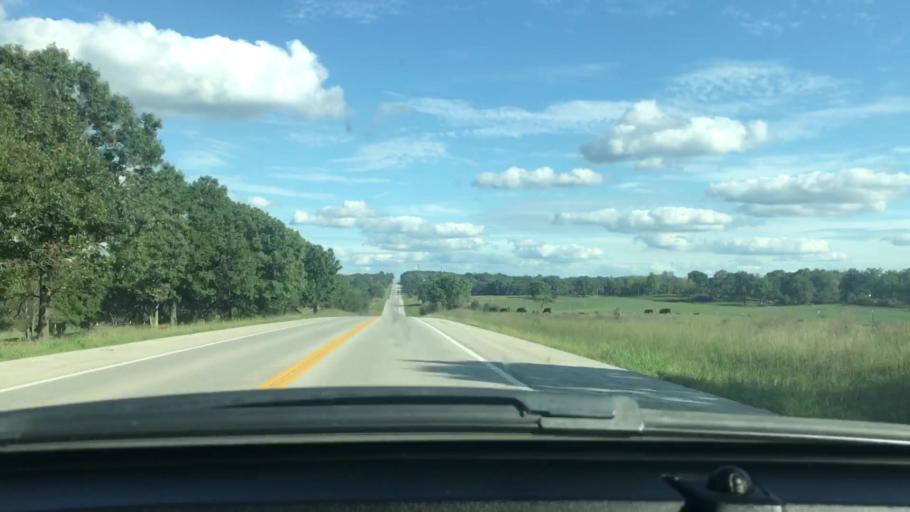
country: US
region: Missouri
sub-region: Howell County
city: West Plains
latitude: 36.6597
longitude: -91.7069
